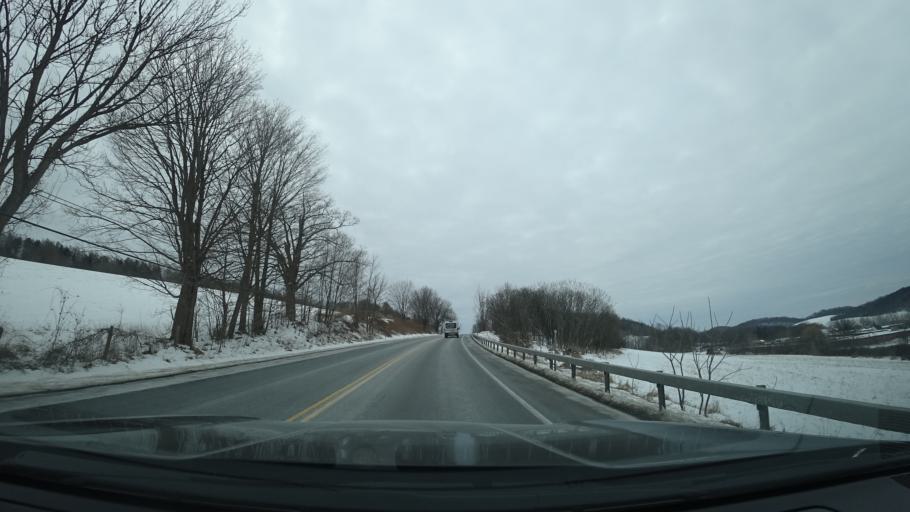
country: US
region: New York
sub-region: Washington County
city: Greenwich
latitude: 43.2049
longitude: -73.4860
